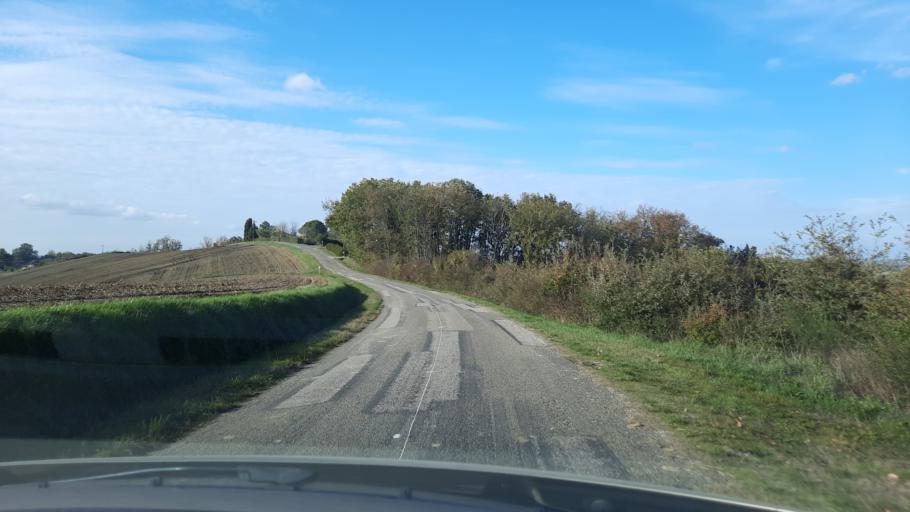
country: FR
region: Midi-Pyrenees
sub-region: Departement du Tarn-et-Garonne
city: Lafrancaise
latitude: 44.1501
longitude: 1.2950
